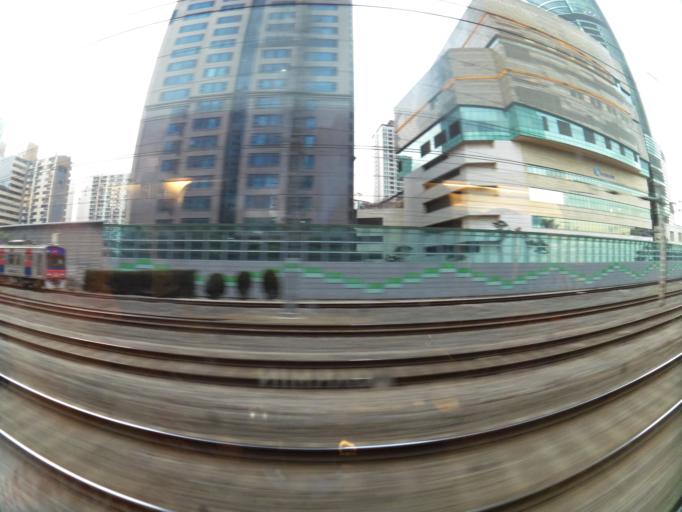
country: KR
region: Gyeonggi-do
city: Kwangmyong
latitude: 37.5076
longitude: 126.8890
